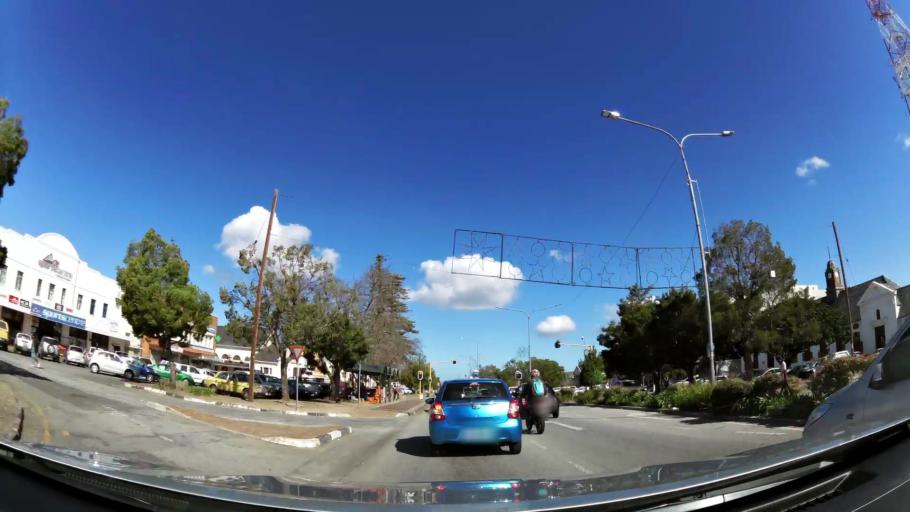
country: ZA
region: Western Cape
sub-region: Eden District Municipality
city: George
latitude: -33.9599
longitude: 22.4559
